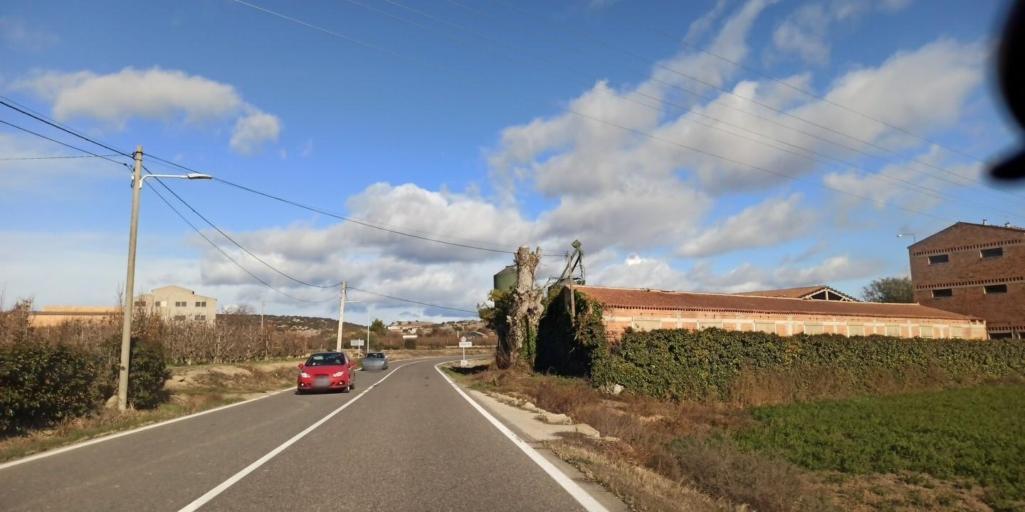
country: ES
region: Catalonia
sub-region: Provincia de Lleida
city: Penelles
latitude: 41.7562
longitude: 0.9610
